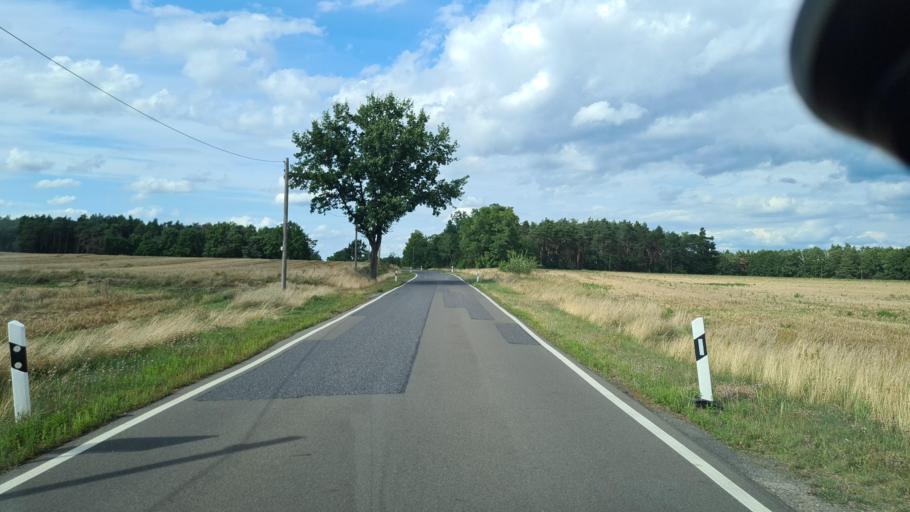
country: DE
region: Brandenburg
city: Neupetershain
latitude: 51.6296
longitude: 14.1614
